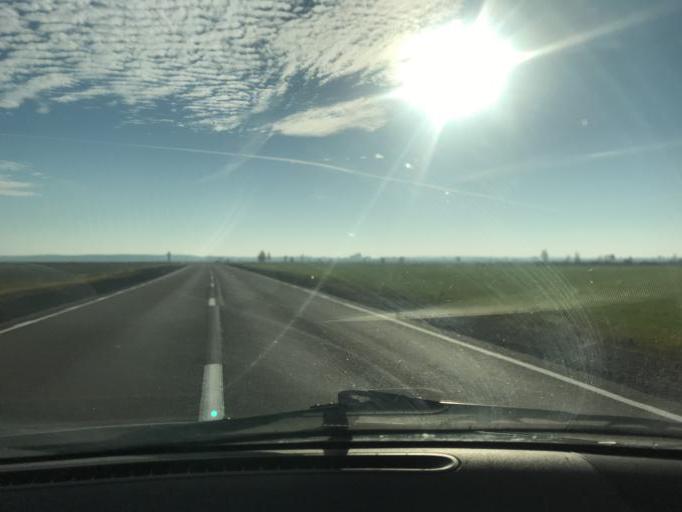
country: BY
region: Brest
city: Drahichyn
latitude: 52.1933
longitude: 25.2524
